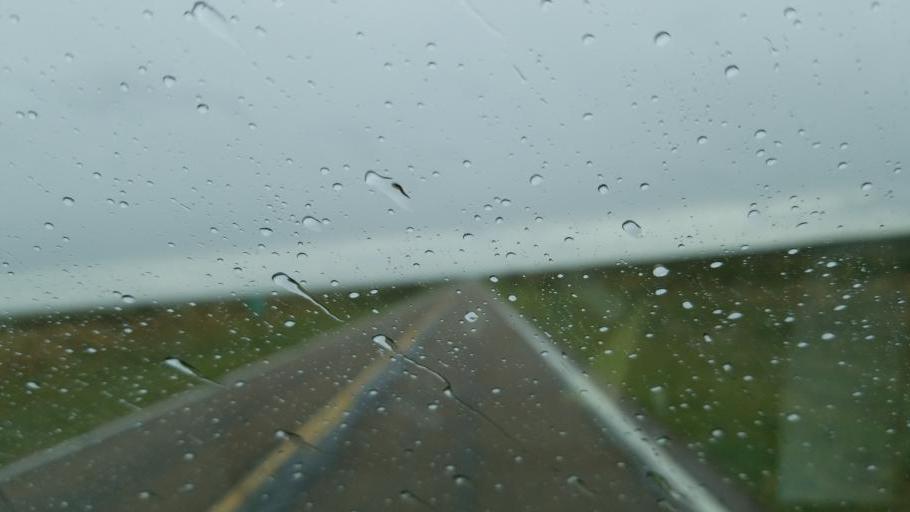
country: US
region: Colorado
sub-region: Lincoln County
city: Hugo
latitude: 38.8496
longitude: -103.1755
